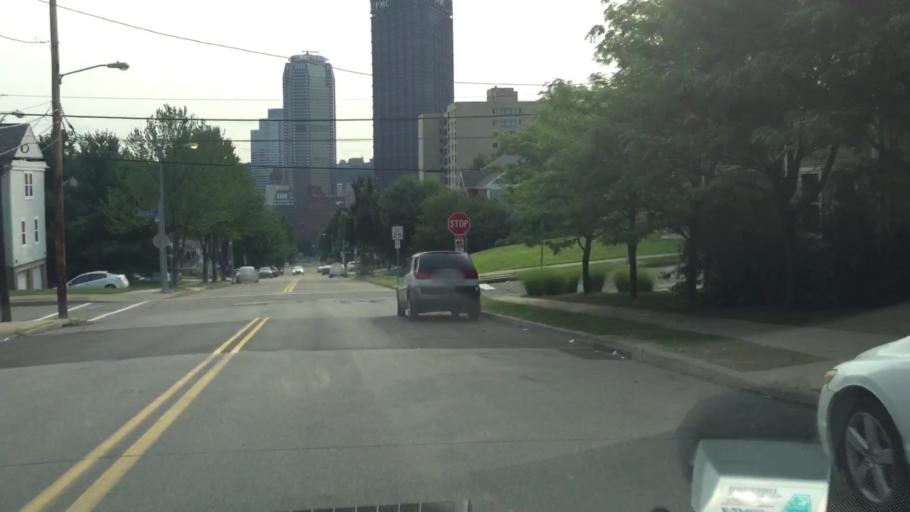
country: US
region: Pennsylvania
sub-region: Allegheny County
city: Pittsburgh
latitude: 40.4445
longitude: -79.9852
